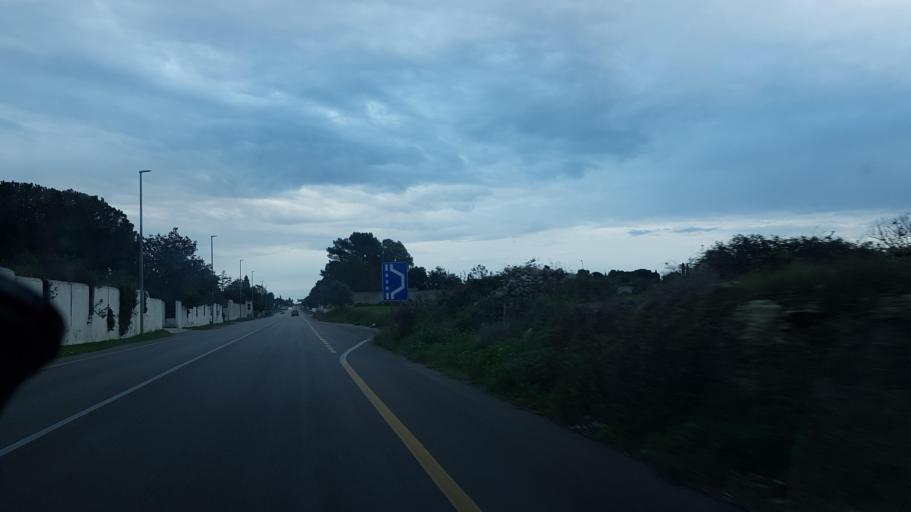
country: IT
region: Apulia
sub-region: Provincia di Lecce
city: Merine
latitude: 40.3421
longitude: 18.2132
